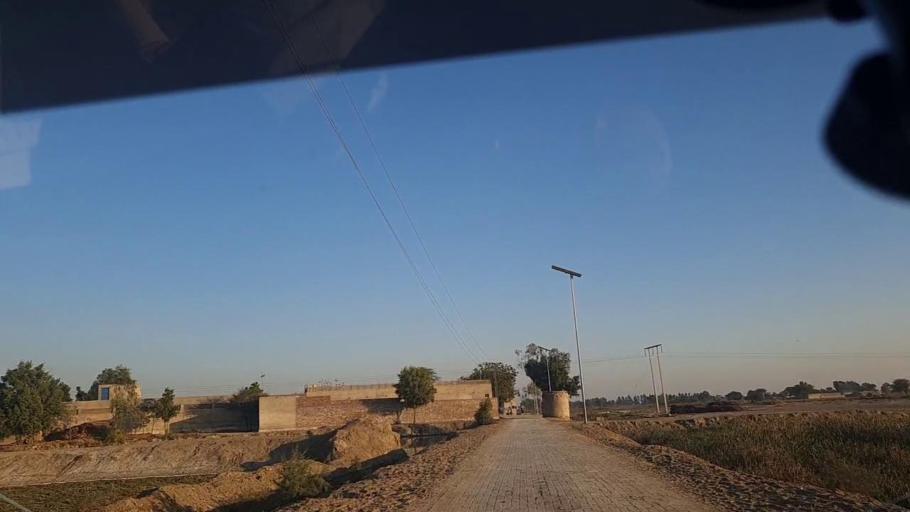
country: PK
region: Sindh
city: Khanpur
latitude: 27.8658
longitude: 69.4249
